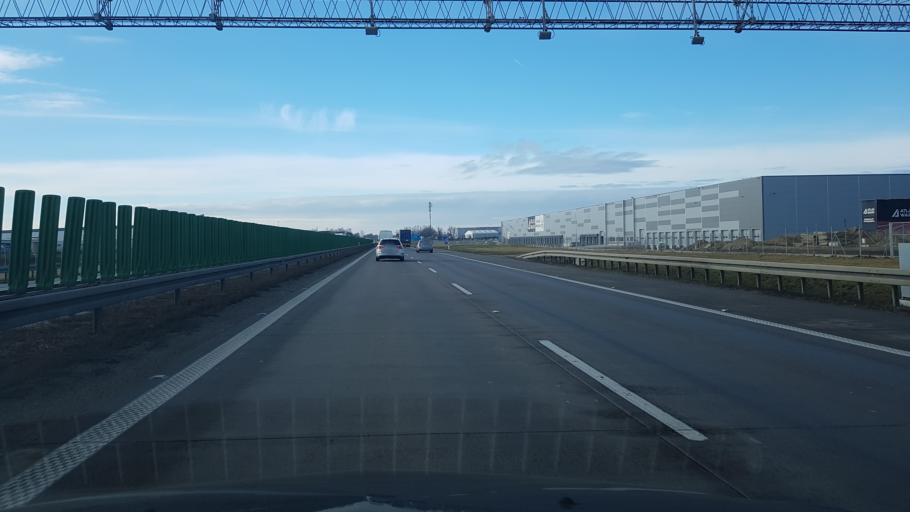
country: PL
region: Lower Silesian Voivodeship
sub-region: Powiat wroclawski
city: Tyniec Maly
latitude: 51.0397
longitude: 16.9055
